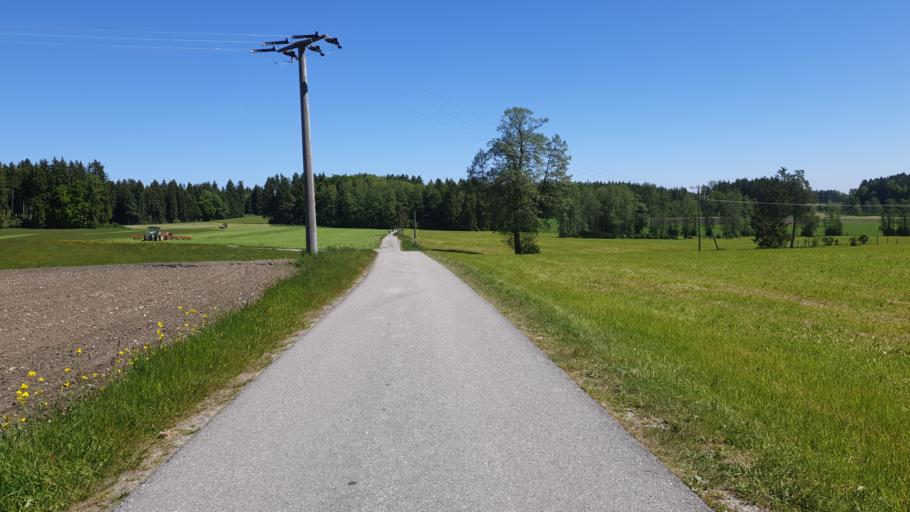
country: DE
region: Bavaria
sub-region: Upper Bavaria
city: Habach
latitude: 47.7508
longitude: 11.2585
